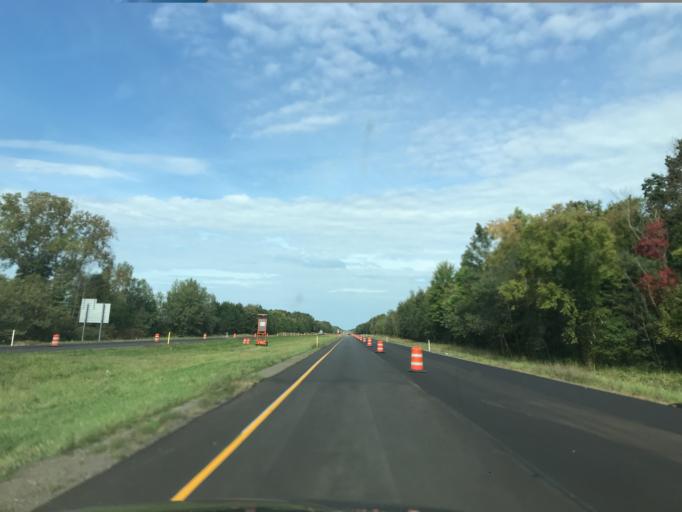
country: US
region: Ohio
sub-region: Ashtabula County
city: Jefferson
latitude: 41.7661
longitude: -80.7216
